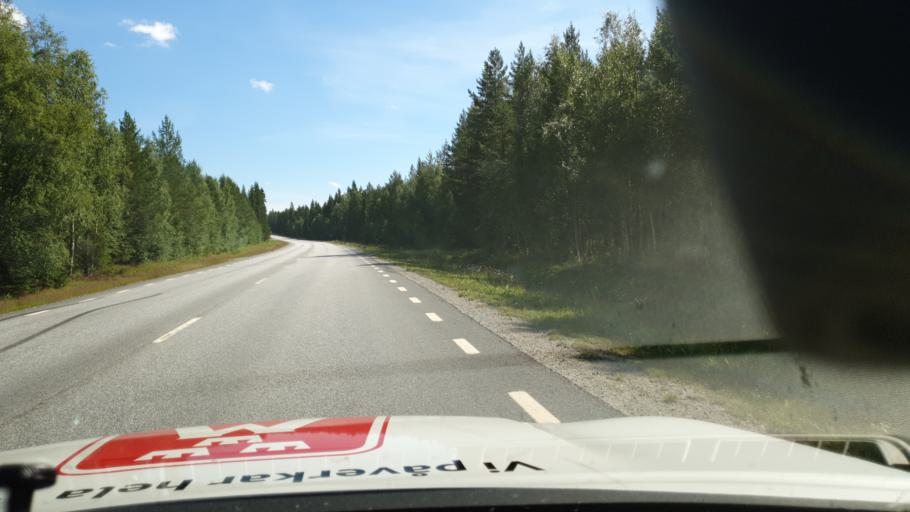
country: SE
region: Vaesterbotten
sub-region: Vannas Kommun
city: Vannasby
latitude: 64.0846
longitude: 19.9778
